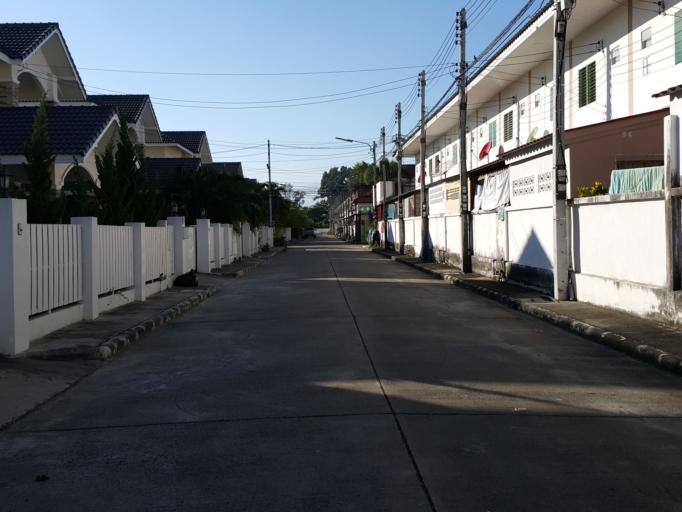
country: TH
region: Chiang Mai
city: San Kamphaeng
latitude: 18.7747
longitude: 99.0855
